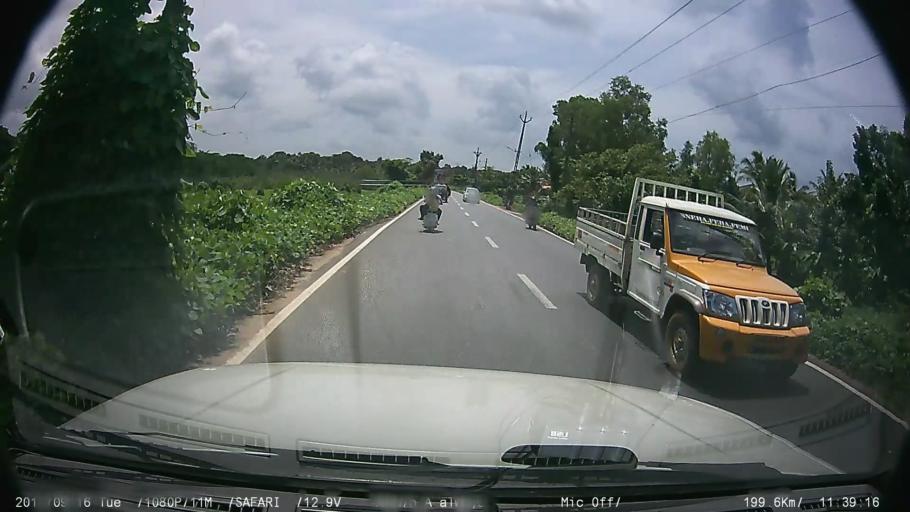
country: IN
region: Kerala
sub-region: Kottayam
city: Changanacheri
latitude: 9.4502
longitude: 76.5468
